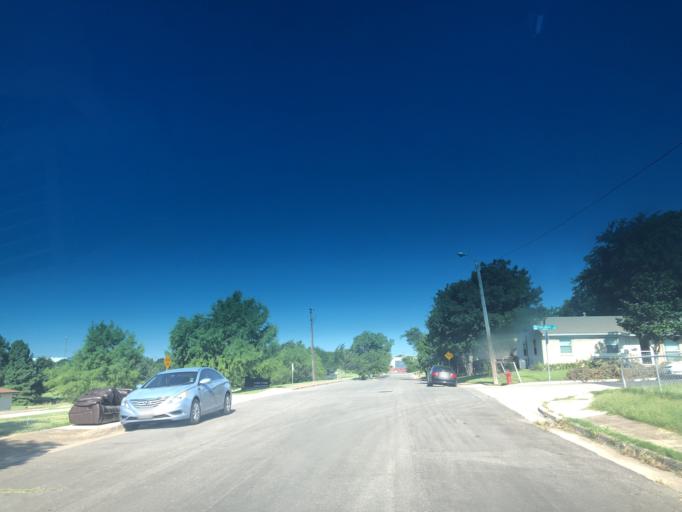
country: US
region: Texas
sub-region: Dallas County
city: Grand Prairie
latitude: 32.7272
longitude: -97.0371
